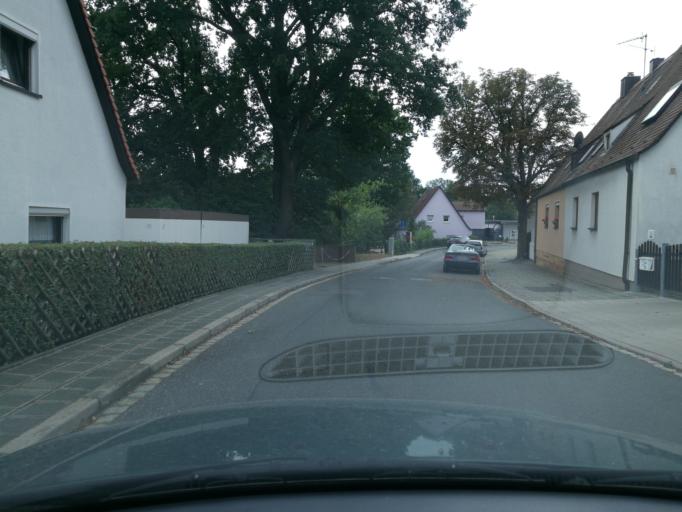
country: DE
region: Bavaria
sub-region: Regierungsbezirk Mittelfranken
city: Furth
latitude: 49.4937
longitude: 10.9647
